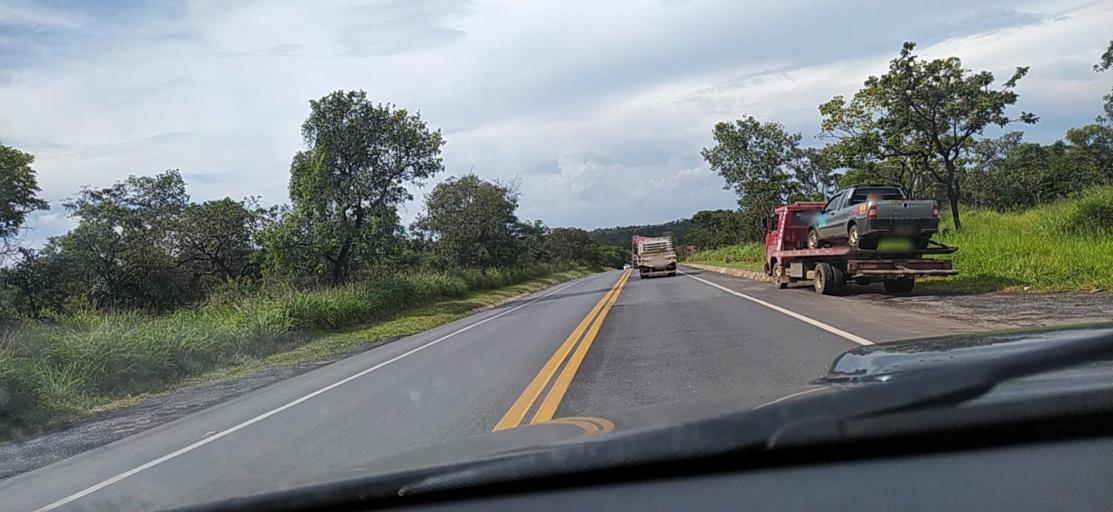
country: BR
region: Minas Gerais
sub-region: Montes Claros
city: Montes Claros
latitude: -16.8603
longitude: -43.8533
